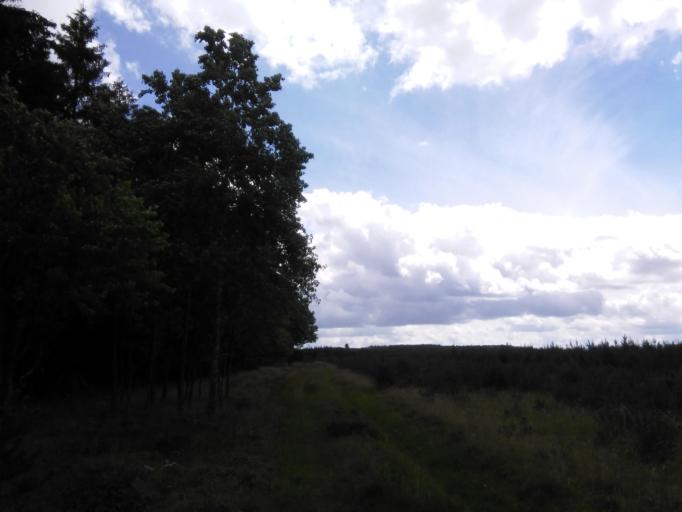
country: DK
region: Central Jutland
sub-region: Silkeborg Kommune
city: Virklund
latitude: 56.0809
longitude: 9.4358
